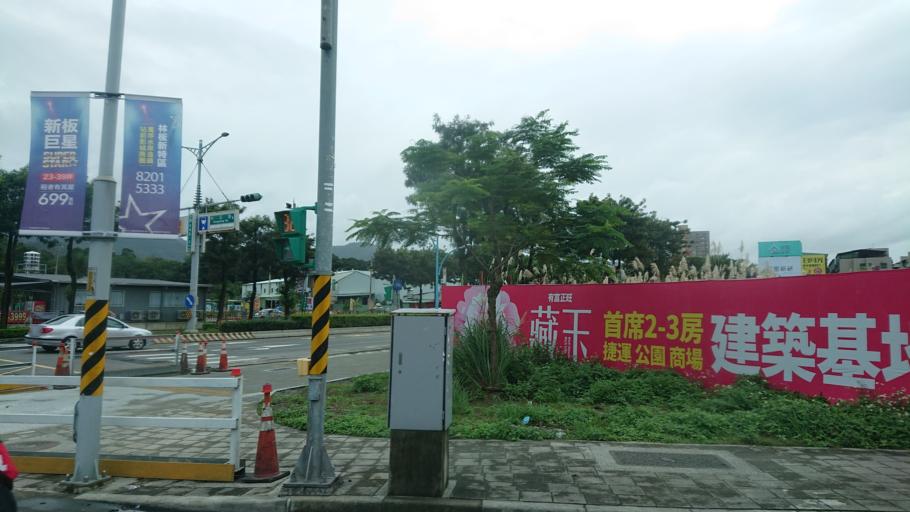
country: TW
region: Taipei
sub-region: Taipei
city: Banqiao
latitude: 24.9758
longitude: 121.4468
